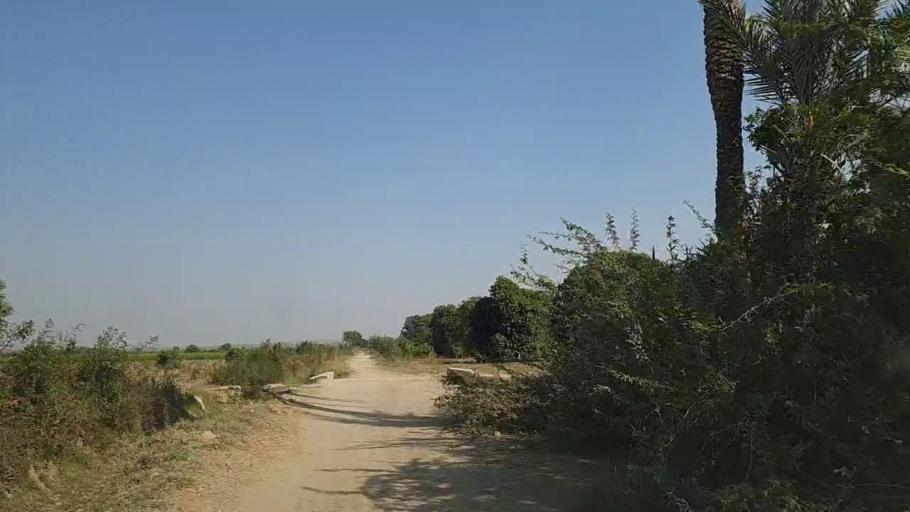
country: PK
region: Sindh
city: Naukot
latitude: 24.8990
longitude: 69.4893
